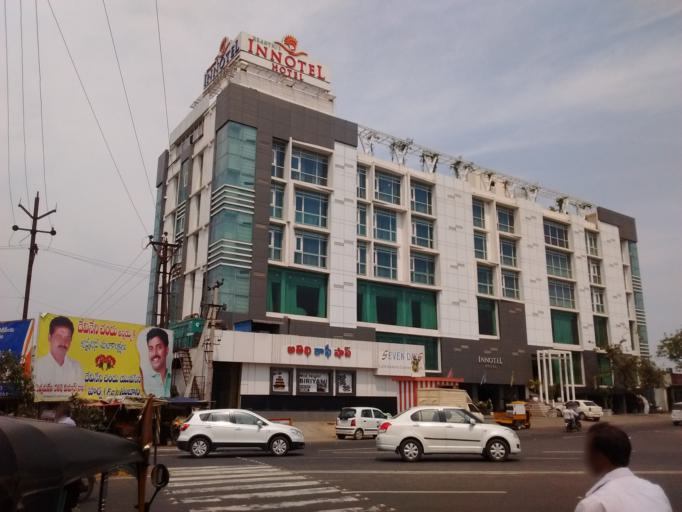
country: IN
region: Andhra Pradesh
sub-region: Krishna
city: Yanamalakuduru
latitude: 16.5240
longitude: 80.6772
